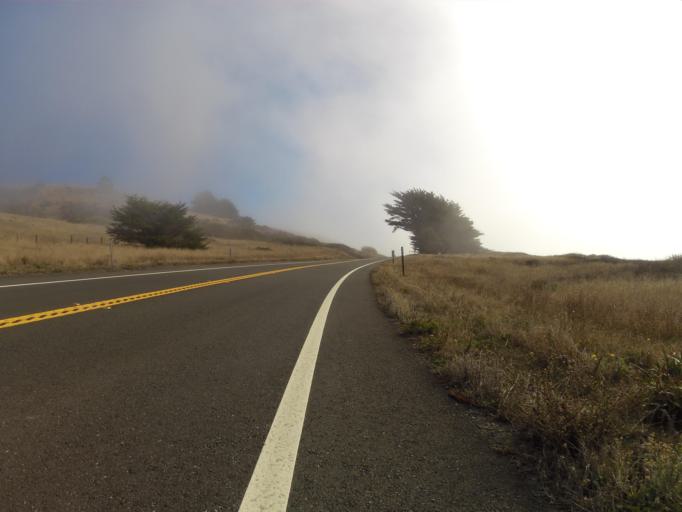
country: US
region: California
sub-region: Sonoma County
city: Sea Ranch
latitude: 38.8637
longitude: -123.6531
